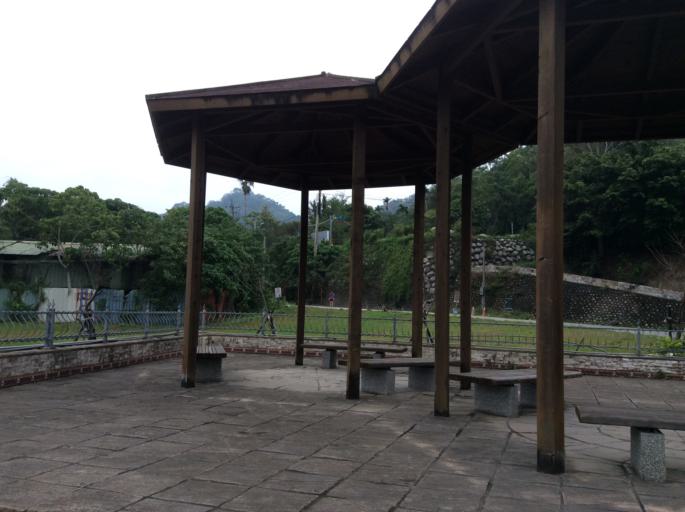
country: TW
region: Taiwan
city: Fengyuan
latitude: 24.2833
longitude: 120.7687
